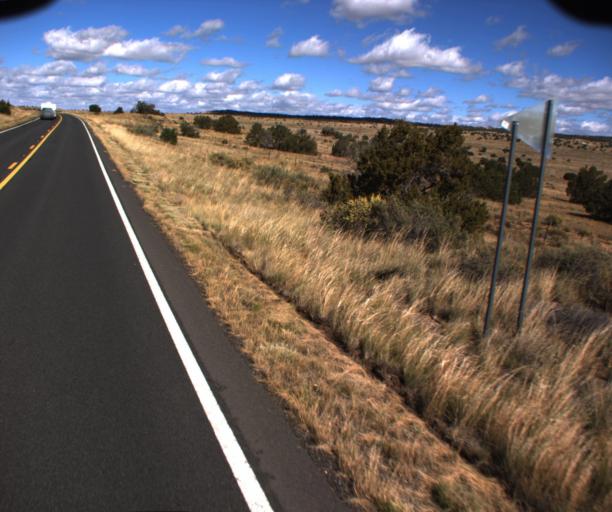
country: US
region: Arizona
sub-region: Apache County
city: Houck
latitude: 35.0247
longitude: -109.2455
